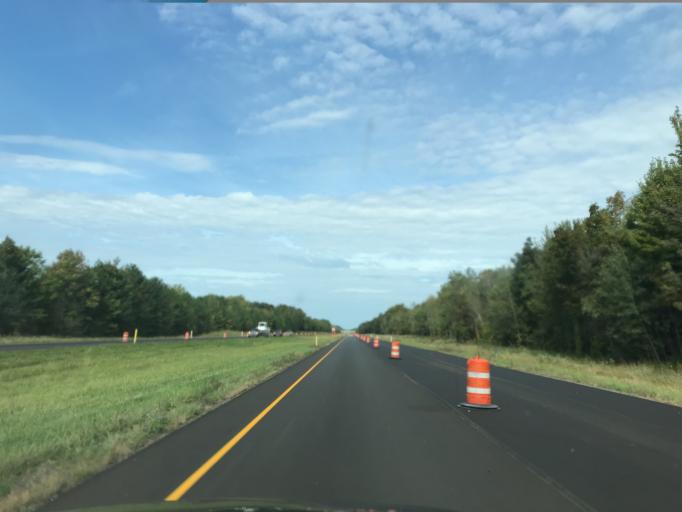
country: US
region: Ohio
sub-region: Ashtabula County
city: Jefferson
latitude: 41.7673
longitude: -80.7224
